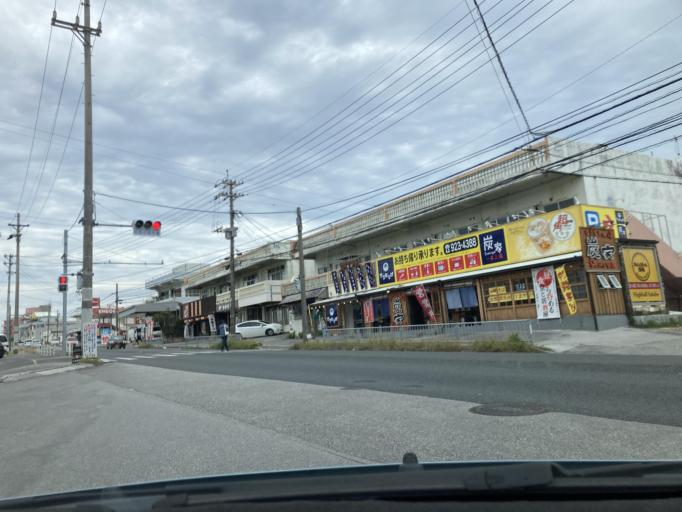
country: JP
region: Okinawa
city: Okinawa
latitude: 26.3835
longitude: 127.7419
